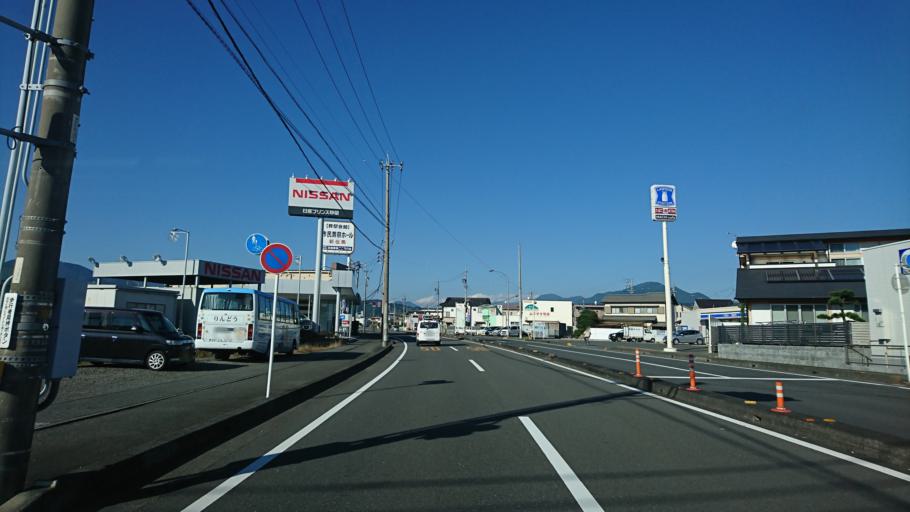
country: JP
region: Shizuoka
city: Shizuoka-shi
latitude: 34.9971
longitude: 138.3645
